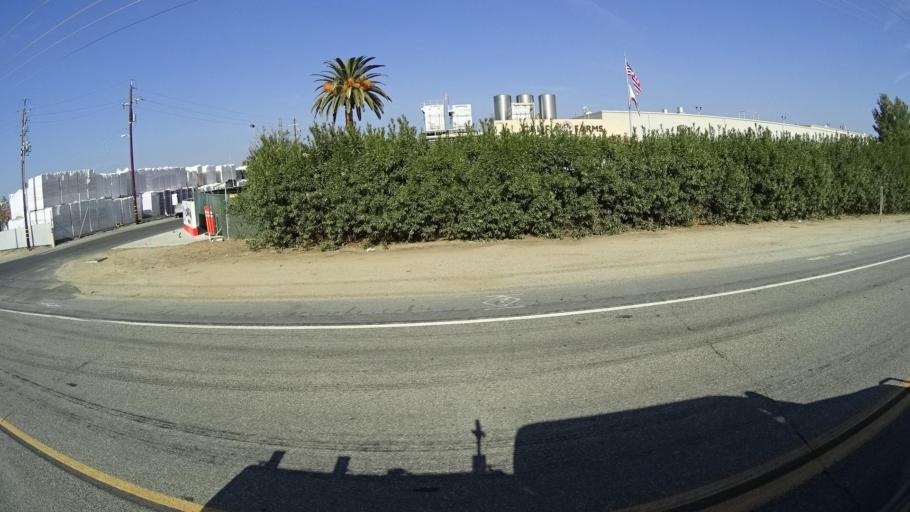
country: US
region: California
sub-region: Kern County
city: Rosedale
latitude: 35.4996
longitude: -119.1436
